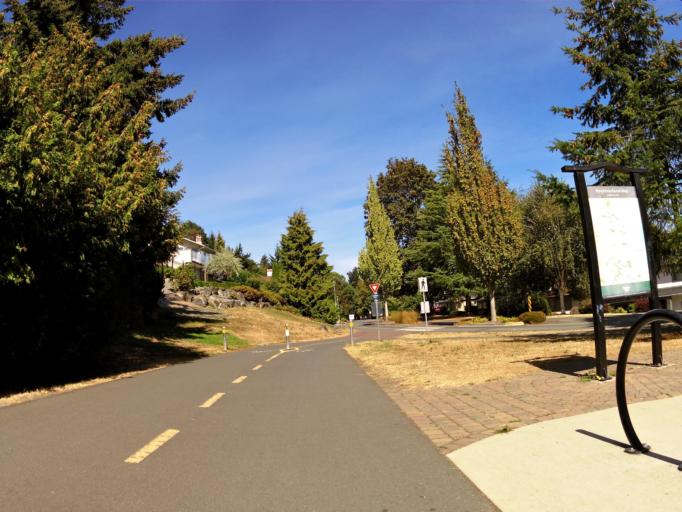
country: CA
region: British Columbia
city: Victoria
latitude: 48.5089
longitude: -123.3661
